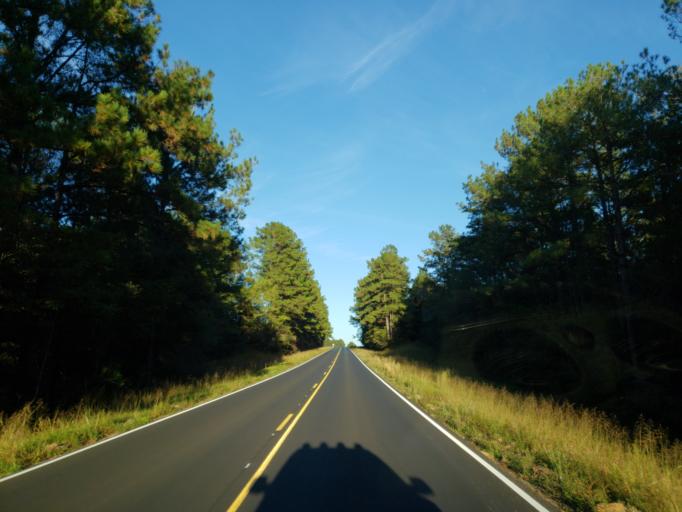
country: US
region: Mississippi
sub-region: Wayne County
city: Belmont
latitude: 31.4164
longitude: -88.5841
